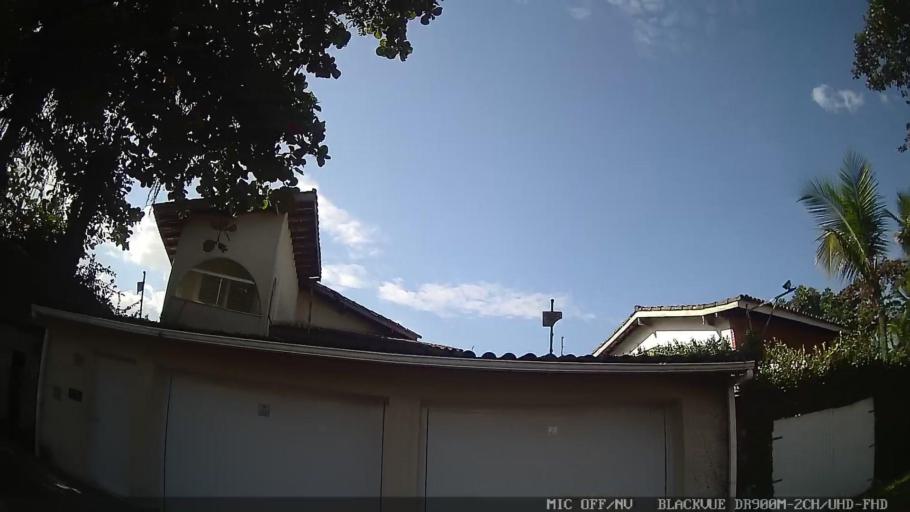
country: BR
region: Sao Paulo
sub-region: Guaruja
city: Guaruja
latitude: -23.9789
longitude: -46.2167
